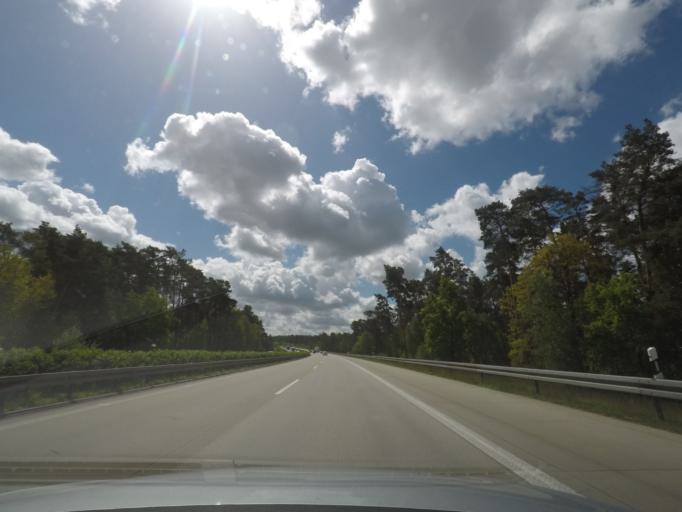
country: DE
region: Brandenburg
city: Bestensee
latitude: 52.2234
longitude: 13.5958
